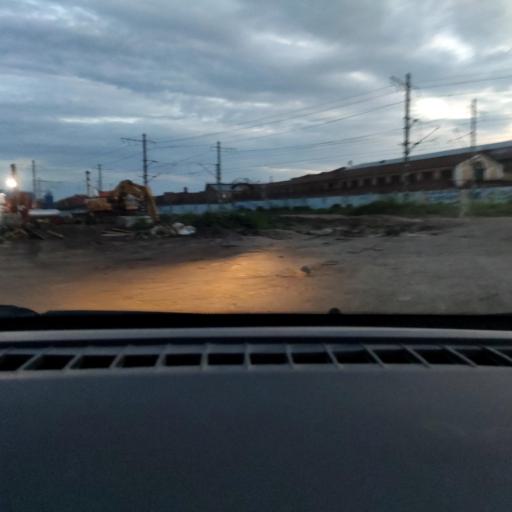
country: RU
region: Perm
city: Perm
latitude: 58.0346
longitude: 56.3071
